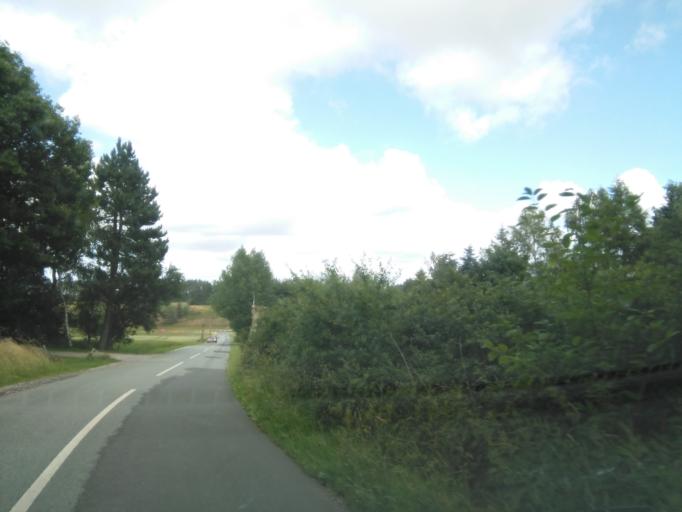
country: DK
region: Central Jutland
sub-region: Syddjurs Kommune
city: Ronde
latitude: 56.2387
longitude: 10.5268
